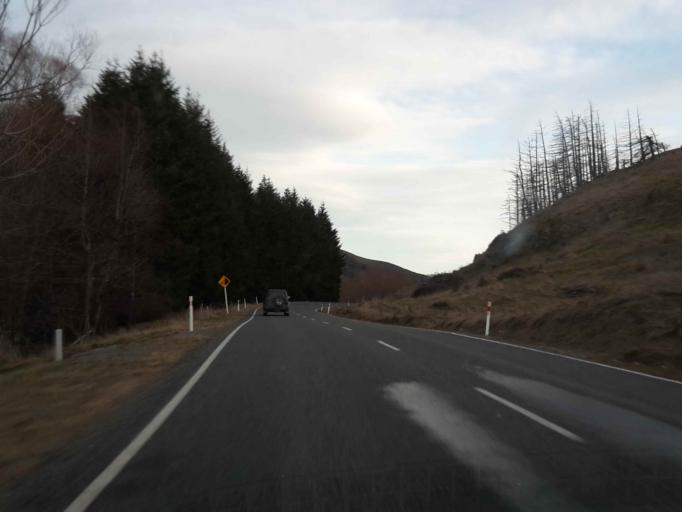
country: NZ
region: Canterbury
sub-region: Timaru District
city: Pleasant Point
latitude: -44.0566
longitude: 170.6758
